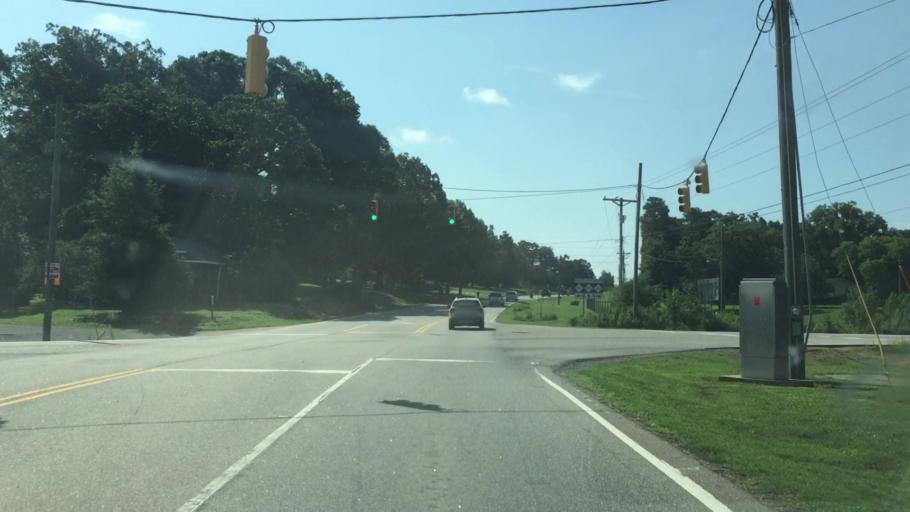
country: US
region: North Carolina
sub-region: Union County
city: Unionville
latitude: 35.1287
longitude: -80.4323
